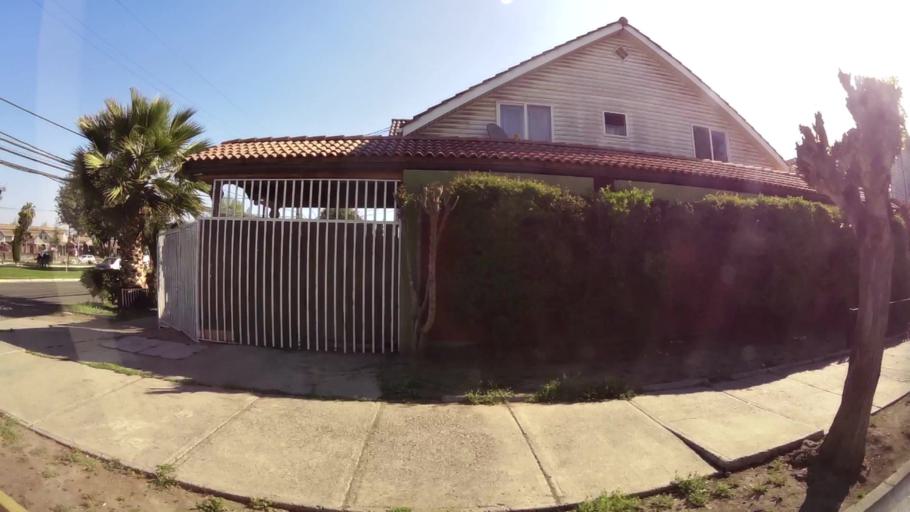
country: CL
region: Santiago Metropolitan
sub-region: Provincia de Santiago
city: Lo Prado
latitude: -33.4884
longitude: -70.7740
